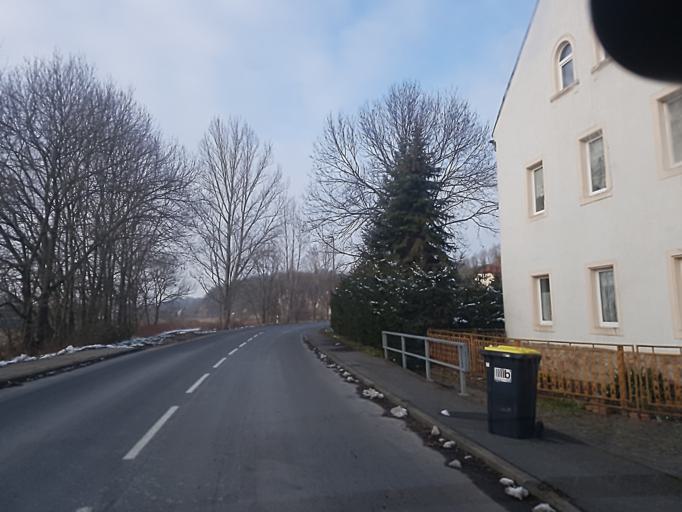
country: DE
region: Saxony
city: Leisnig
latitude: 51.1669
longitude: 12.9235
